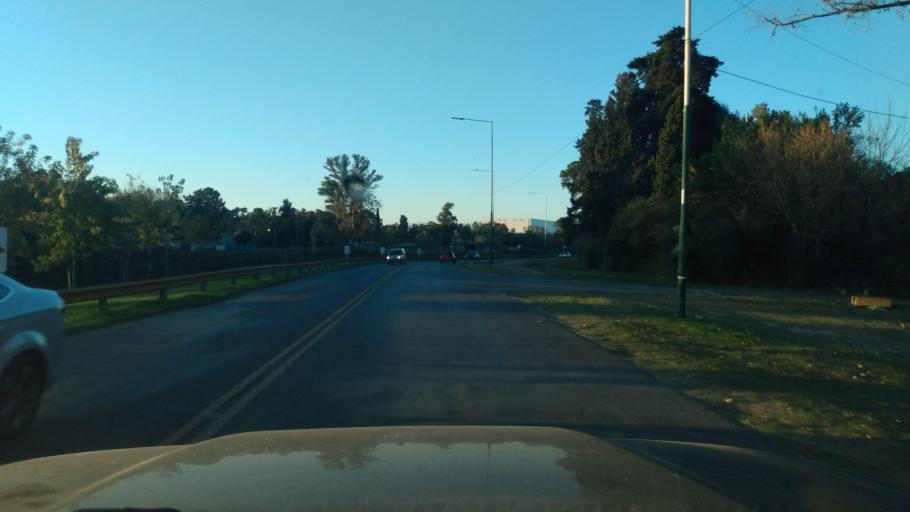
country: AR
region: Buenos Aires
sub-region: Partido de Merlo
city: Merlo
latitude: -34.6387
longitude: -58.7315
